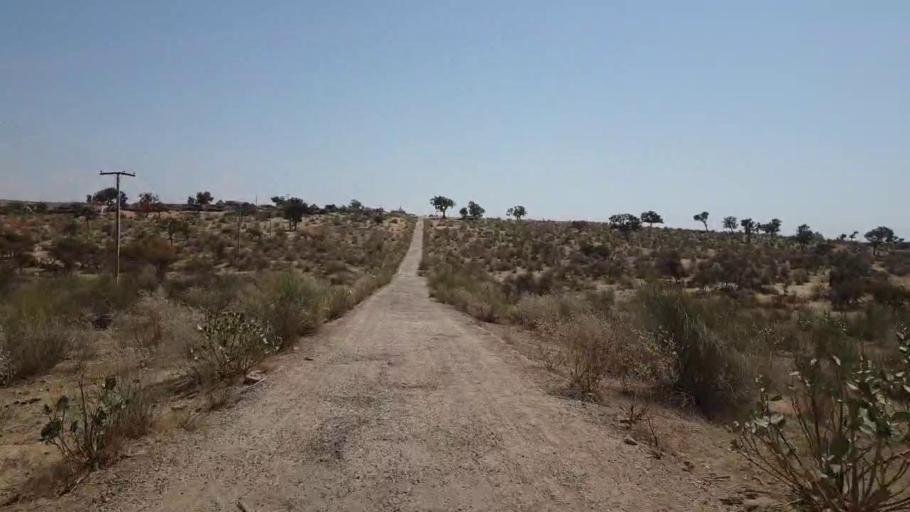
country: PK
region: Sindh
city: Nabisar
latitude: 25.1074
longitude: 69.9016
